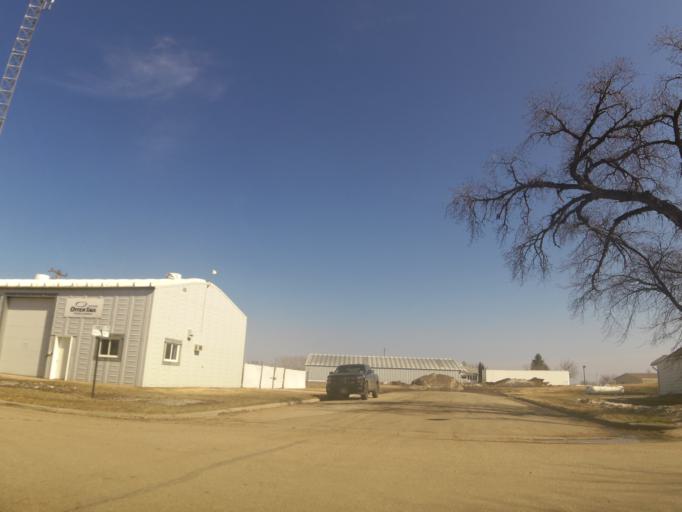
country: US
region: North Dakota
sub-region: Walsh County
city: Grafton
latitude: 48.2905
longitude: -97.3700
